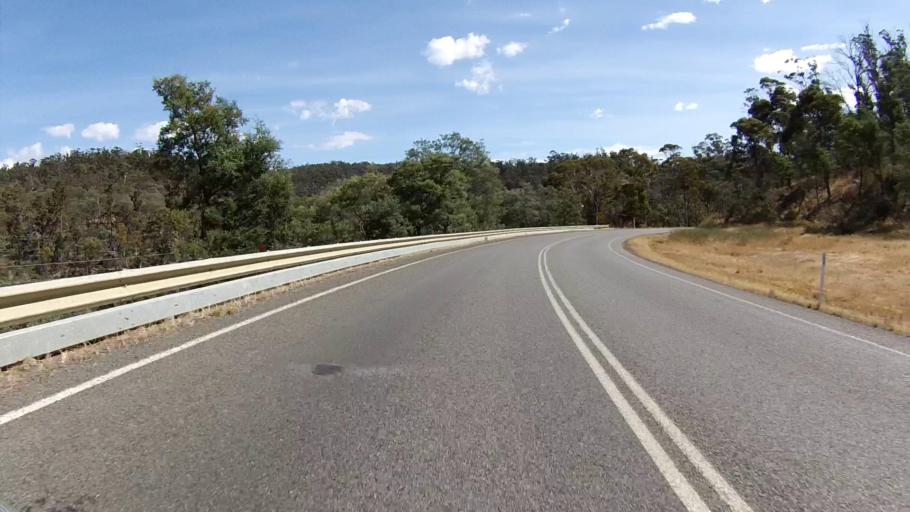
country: AU
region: Tasmania
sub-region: Sorell
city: Sorell
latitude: -42.6104
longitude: 147.6702
